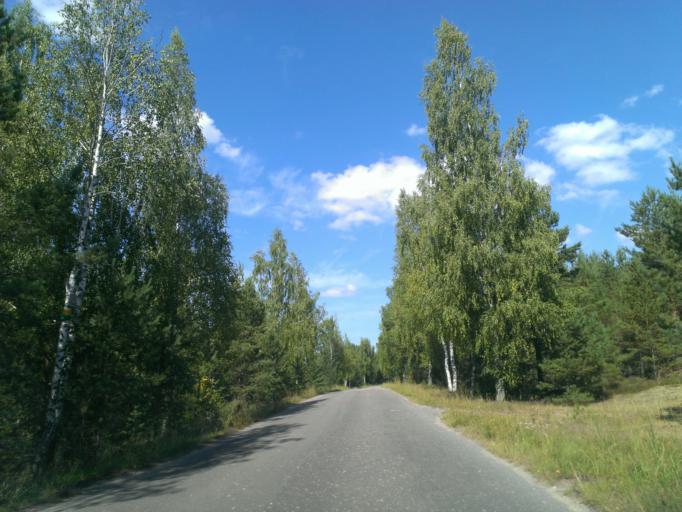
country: LV
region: Adazi
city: Adazi
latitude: 57.1127
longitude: 24.3630
